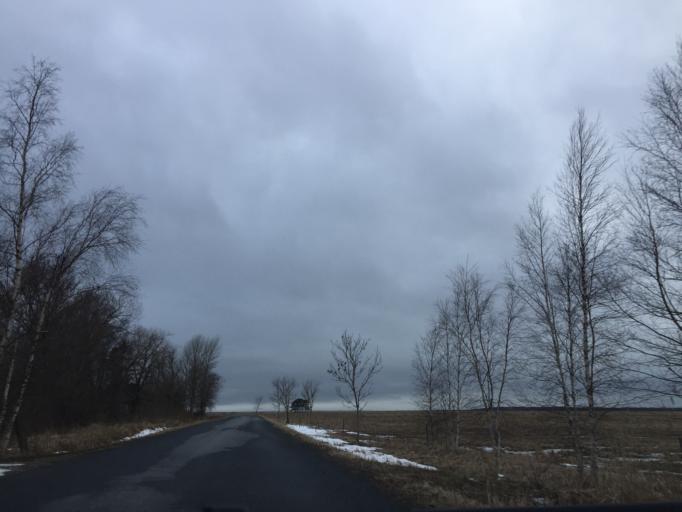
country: EE
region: Laeaene
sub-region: Haapsalu linn
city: Haapsalu
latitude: 58.8008
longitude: 23.5107
